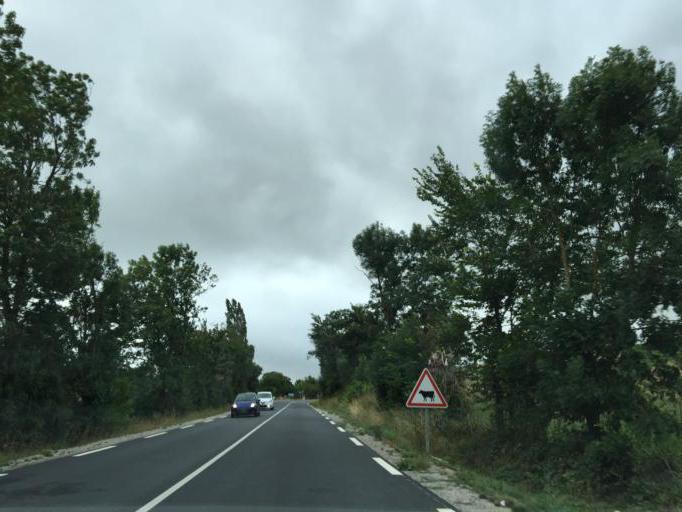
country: FR
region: Midi-Pyrenees
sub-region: Departement de l'Aveyron
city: Severac-le-Chateau
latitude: 44.2391
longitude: 2.9642
